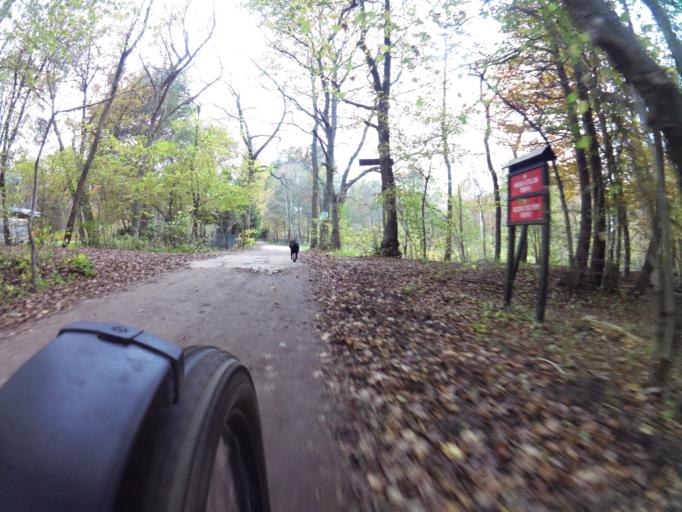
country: PL
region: Pomeranian Voivodeship
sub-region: Powiat pucki
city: Krokowa
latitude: 54.8291
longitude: 18.1090
